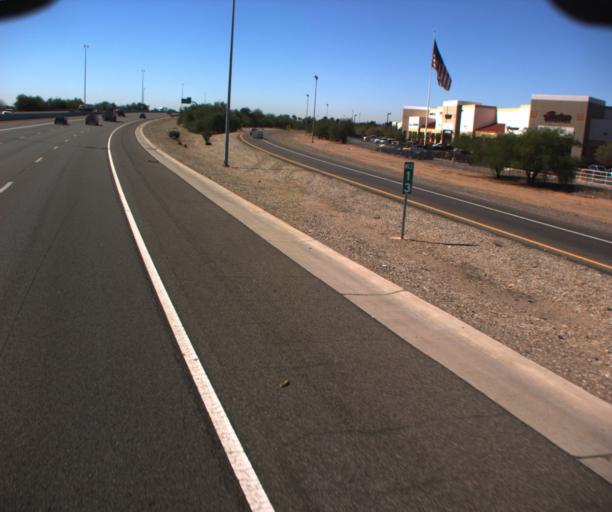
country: US
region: Arizona
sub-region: Maricopa County
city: Peoria
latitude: 33.6137
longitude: -112.2408
